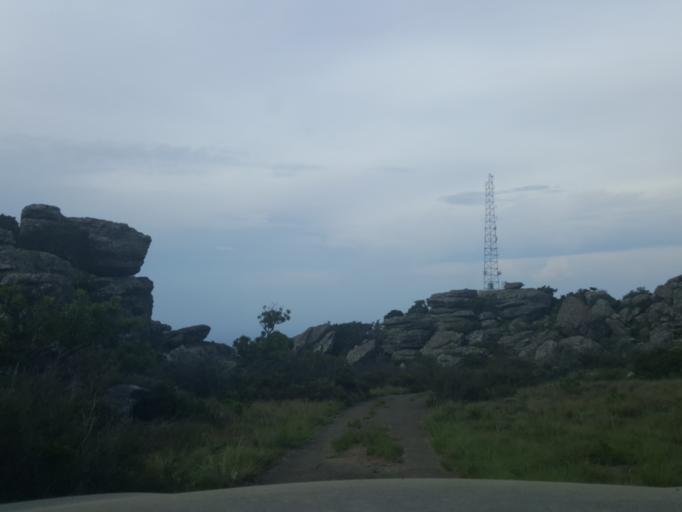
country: ZA
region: Limpopo
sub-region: Mopani District Municipality
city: Hoedspruit
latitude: -24.5395
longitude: 30.8706
